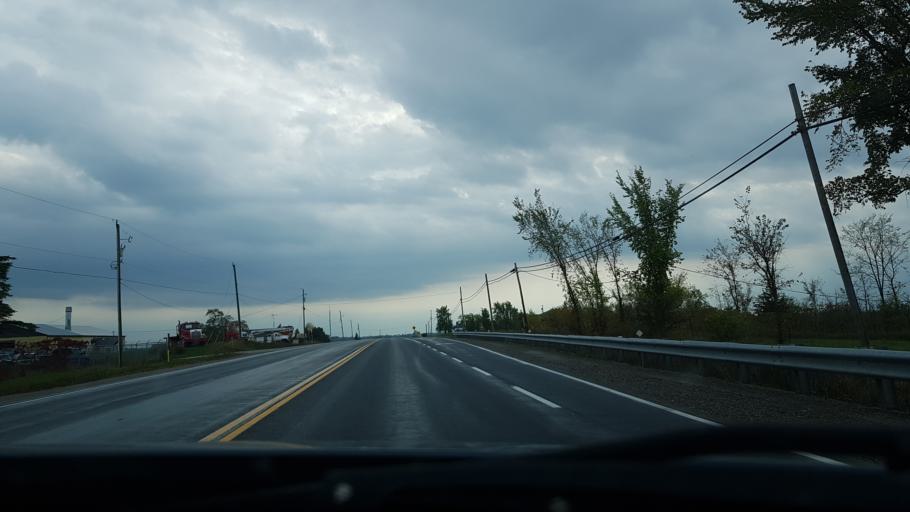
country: CA
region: Ontario
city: Omemee
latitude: 44.4219
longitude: -78.7818
